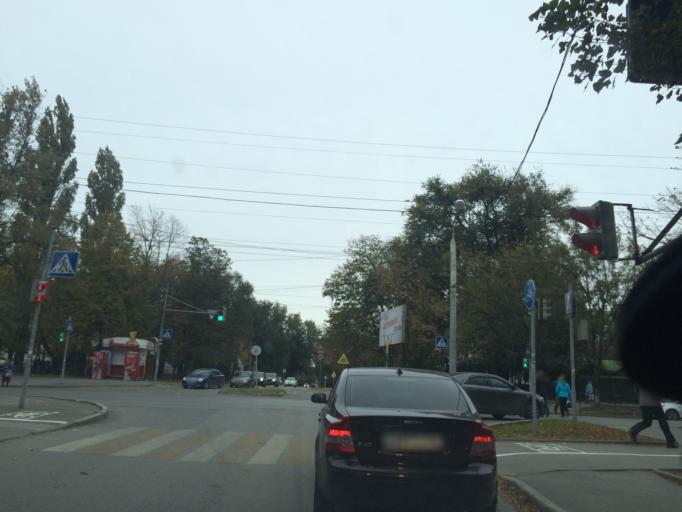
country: RU
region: Rostov
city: Rostov-na-Donu
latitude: 47.2075
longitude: 39.6235
